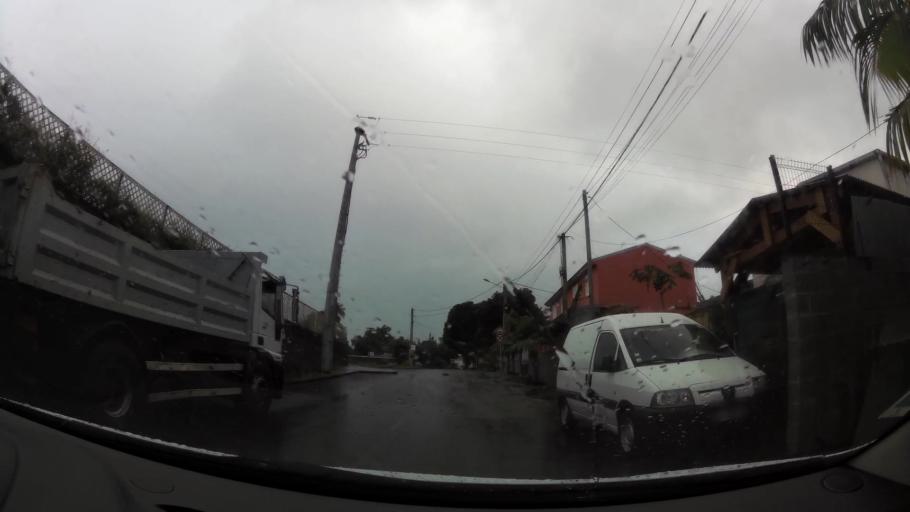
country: RE
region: Reunion
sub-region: Reunion
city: Saint-Benoit
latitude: -21.0301
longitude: 55.6875
